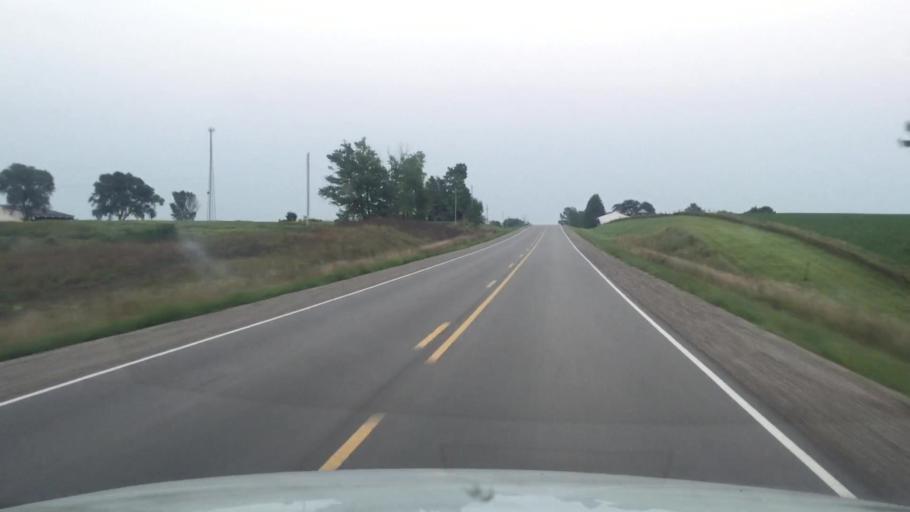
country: US
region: Iowa
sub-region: Marion County
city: Melcher-Dallas
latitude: 41.1896
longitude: -93.4094
